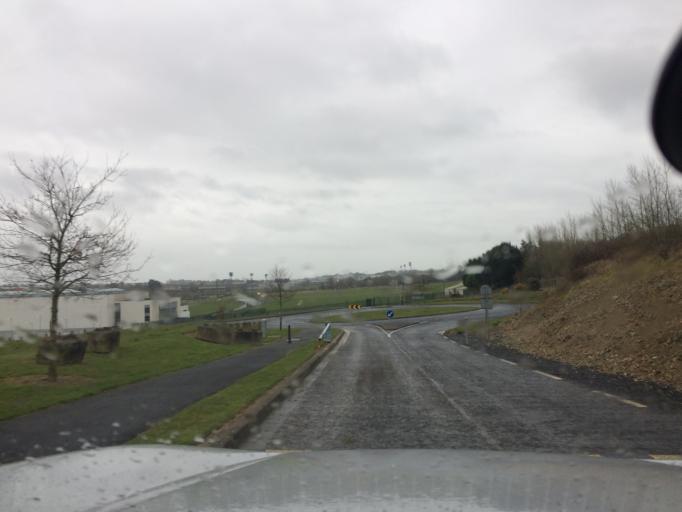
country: IE
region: Munster
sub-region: Waterford
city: Waterford
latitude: 52.2521
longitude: -7.1832
